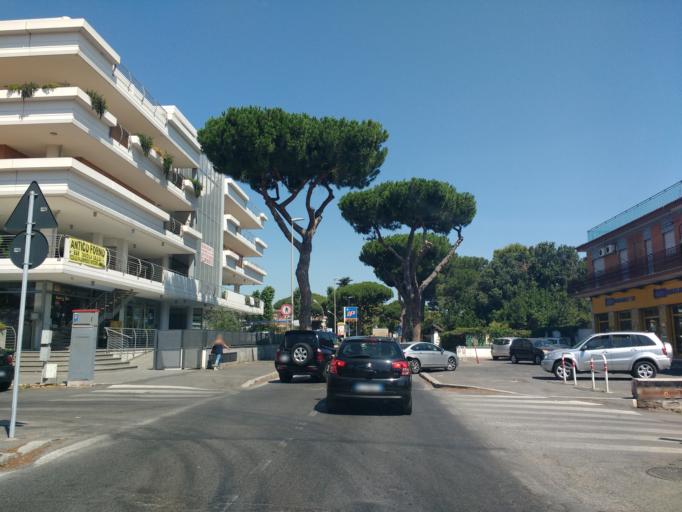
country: IT
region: Latium
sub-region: Citta metropolitana di Roma Capitale
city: Acilia-Castel Fusano-Ostia Antica
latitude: 41.7806
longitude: 12.3669
